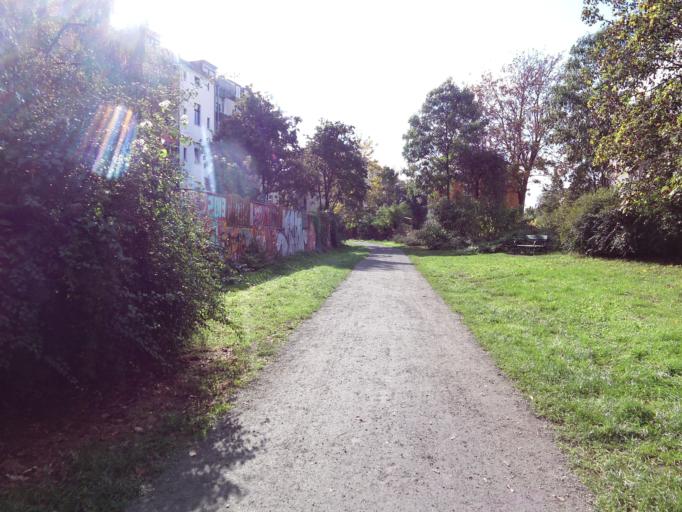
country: DE
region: Saxony
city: Leipzig
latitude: 51.3324
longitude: 12.3253
